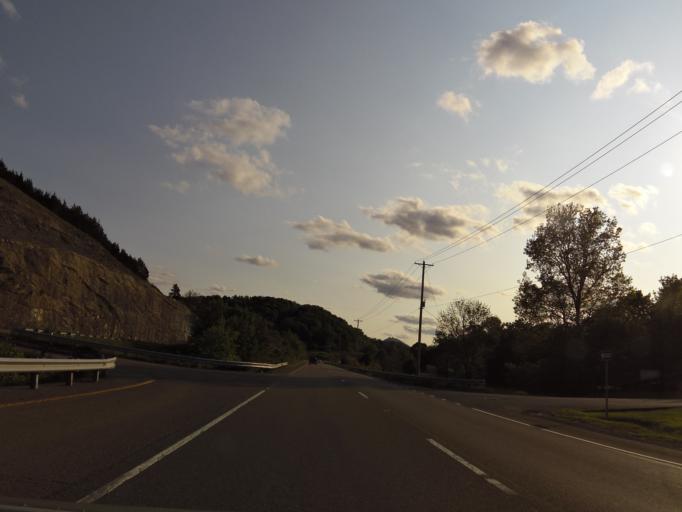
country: US
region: Virginia
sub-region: Tazewell County
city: Claypool Hill
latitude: 37.0441
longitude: -81.7853
